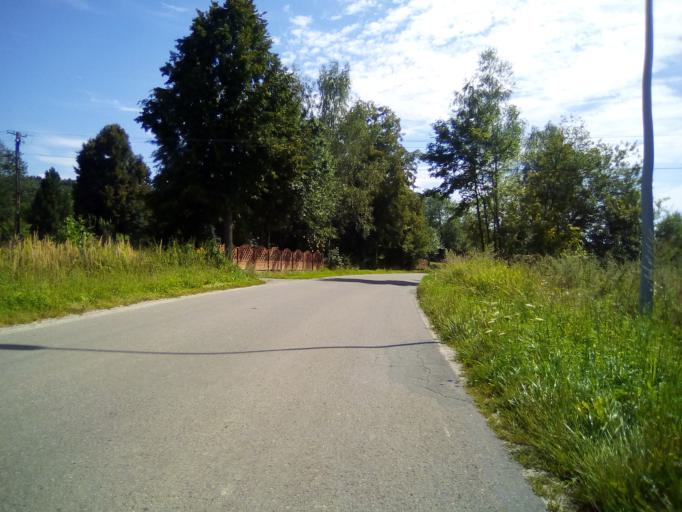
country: PL
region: Subcarpathian Voivodeship
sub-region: Powiat strzyzowski
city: Konieczkowa
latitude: 49.8231
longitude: 21.9265
